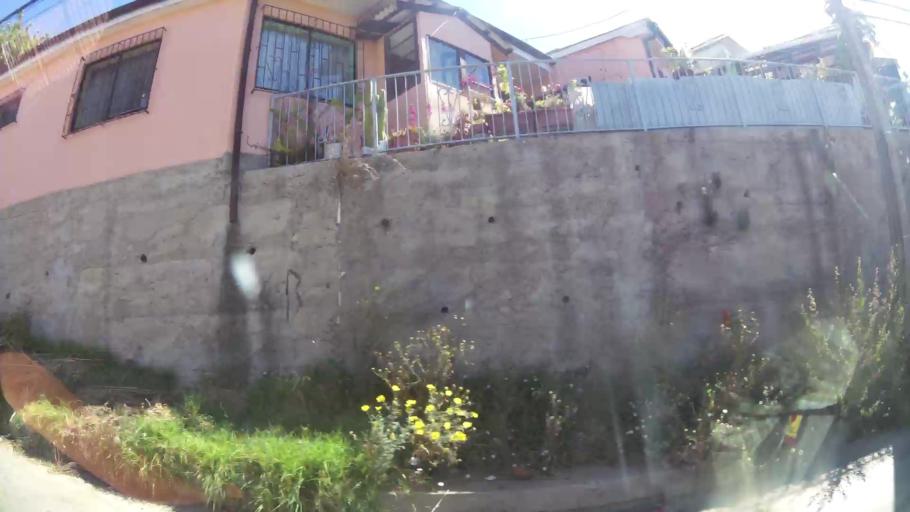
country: CL
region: Valparaiso
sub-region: Provincia de Valparaiso
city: Vina del Mar
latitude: -33.0417
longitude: -71.5665
